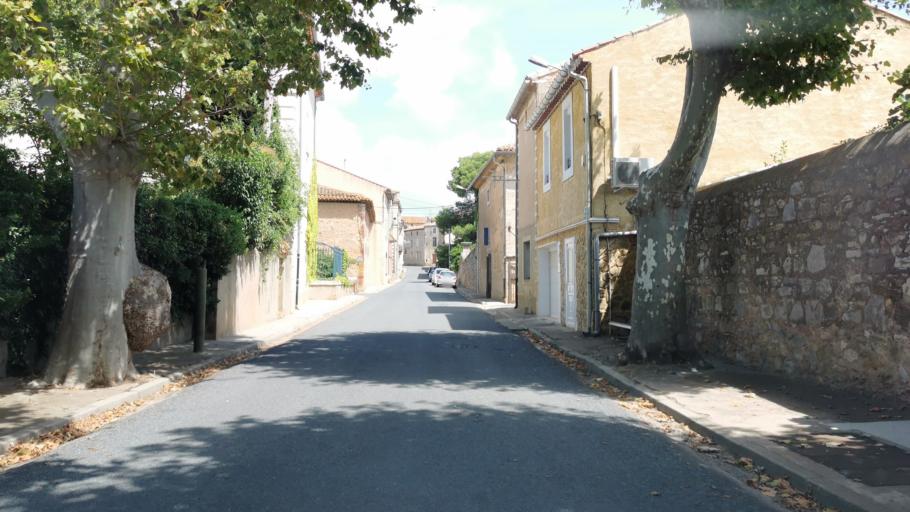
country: FR
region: Languedoc-Roussillon
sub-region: Departement de l'Aude
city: Bizanet
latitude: 43.1621
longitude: 2.8688
